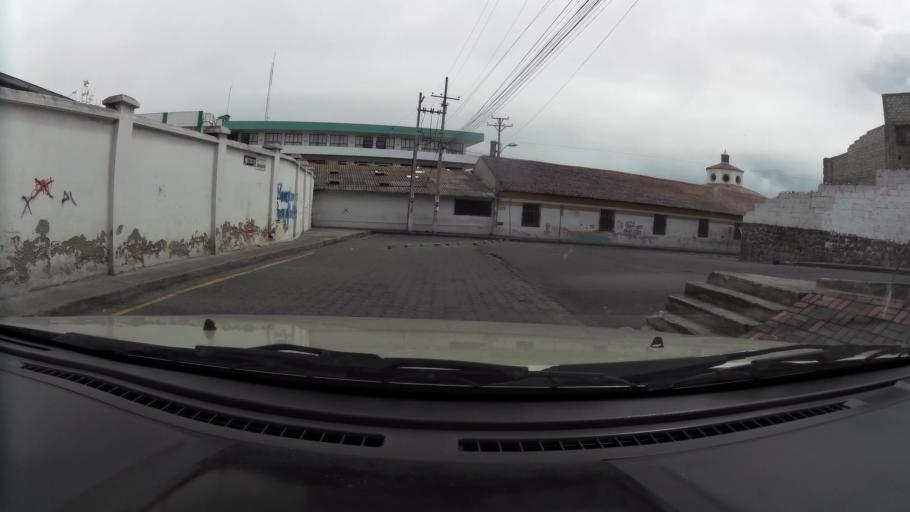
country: EC
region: Cotopaxi
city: Latacunga
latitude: -0.9318
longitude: -78.6175
